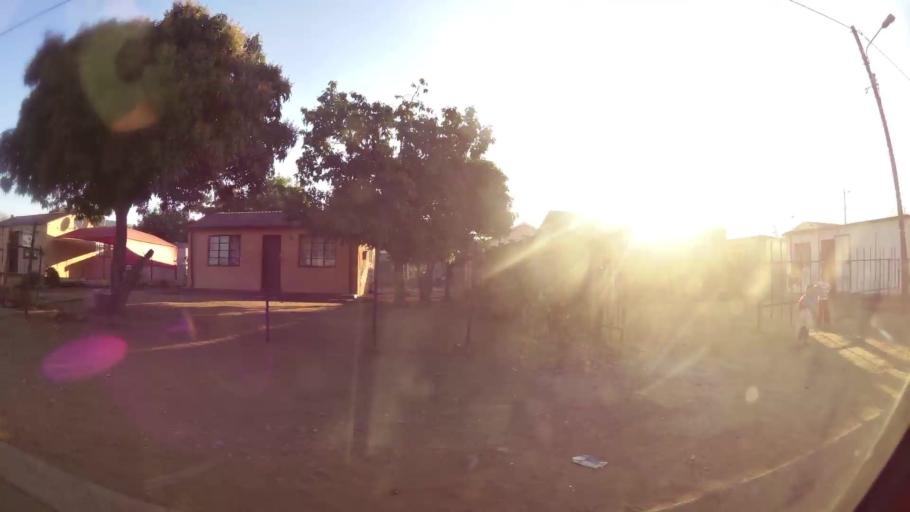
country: ZA
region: North-West
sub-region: Bojanala Platinum District Municipality
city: Rustenburg
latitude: -25.6310
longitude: 27.2123
